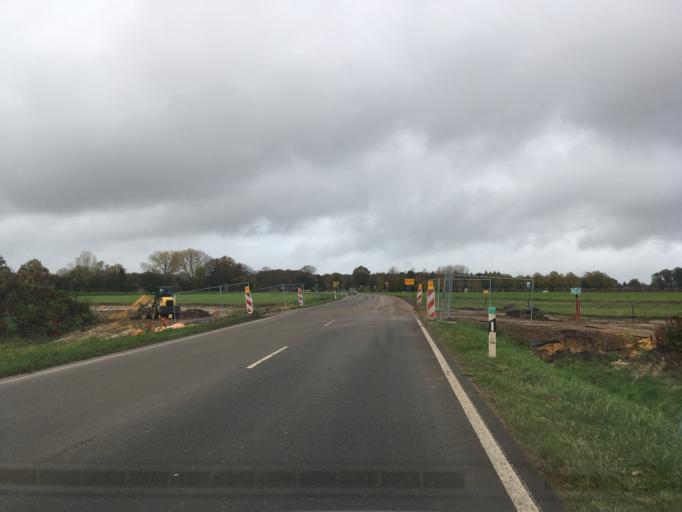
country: DE
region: North Rhine-Westphalia
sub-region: Regierungsbezirk Munster
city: Velen
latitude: 51.8812
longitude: 6.9978
